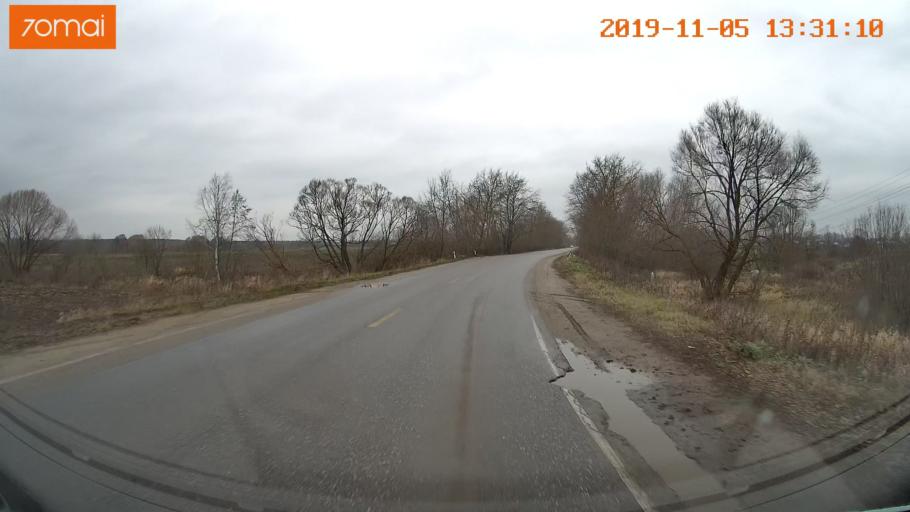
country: RU
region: Ivanovo
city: Shuya
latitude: 56.8729
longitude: 41.3924
